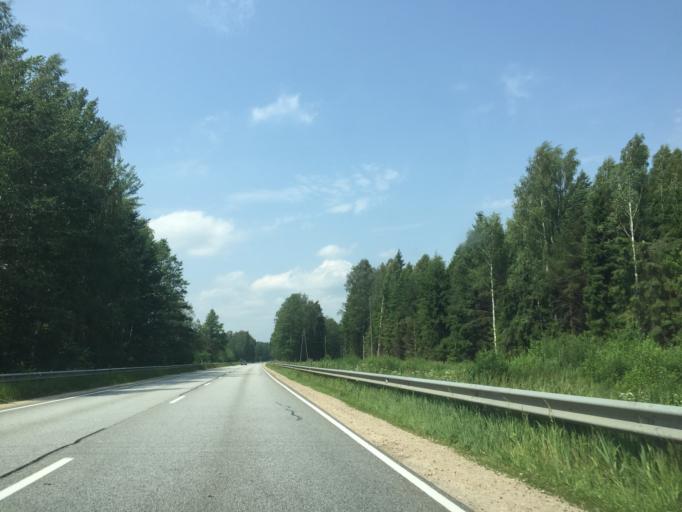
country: LV
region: Kekava
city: Balozi
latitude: 56.8233
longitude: 24.0756
